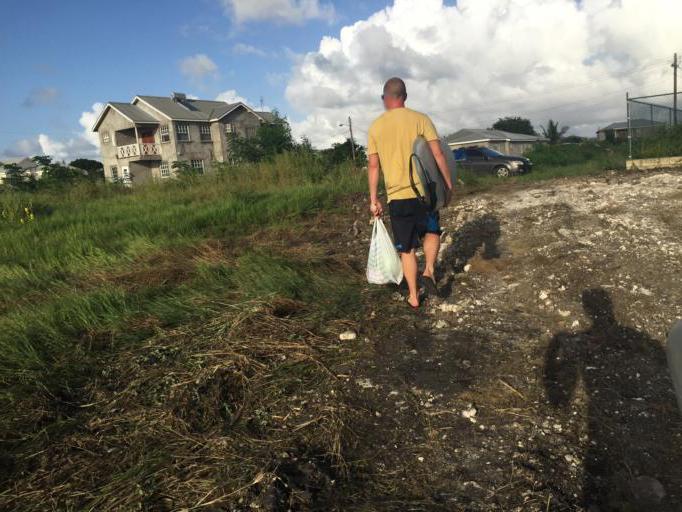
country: BB
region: Saint Lucy
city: Checker Hall
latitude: 13.2937
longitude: -59.6480
